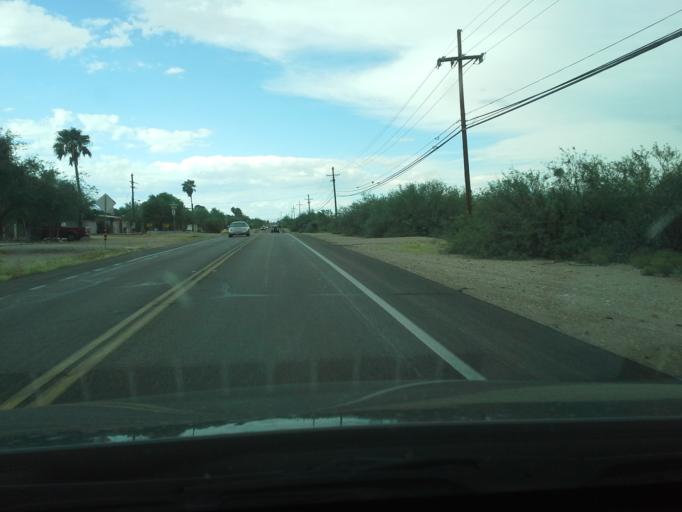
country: US
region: Arizona
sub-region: Pima County
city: South Tucson
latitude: 32.2146
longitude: -111.0203
